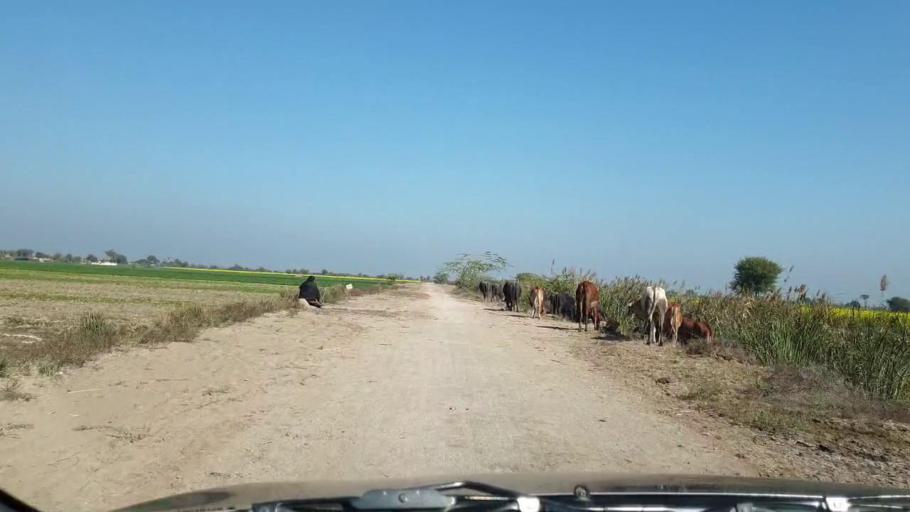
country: PK
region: Sindh
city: Sinjhoro
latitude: 25.9659
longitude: 68.7521
